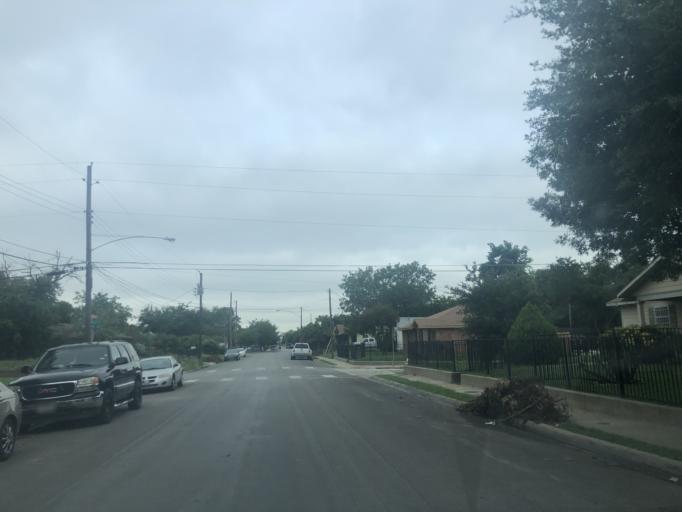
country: US
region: Texas
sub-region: Dallas County
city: Dallas
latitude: 32.7870
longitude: -96.8459
